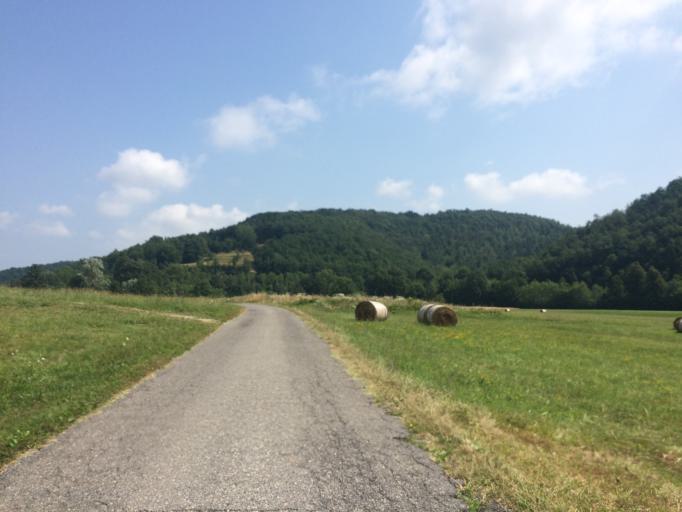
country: IT
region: Liguria
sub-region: Provincia di Savona
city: Piana Crixia
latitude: 44.4715
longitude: 8.3512
